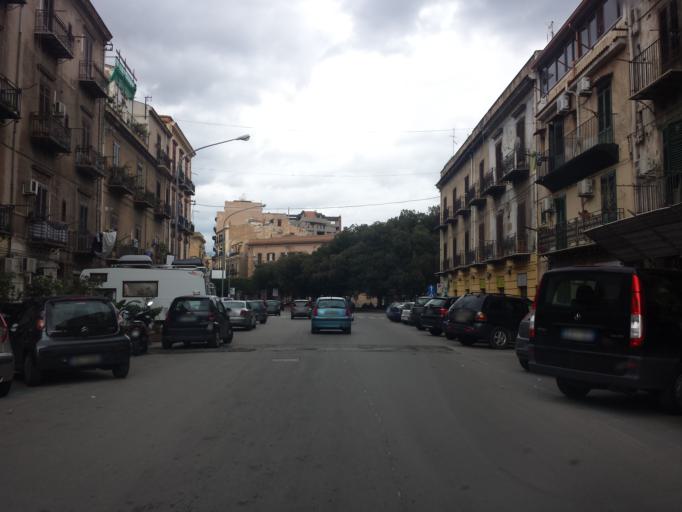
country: IT
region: Sicily
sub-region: Palermo
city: Palermo
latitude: 38.1204
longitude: 13.3529
